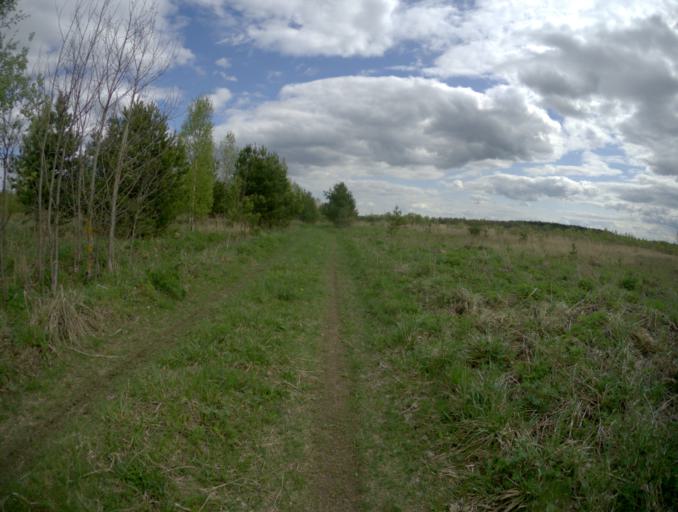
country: RU
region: Vladimir
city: Golovino
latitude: 55.9448
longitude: 40.4111
